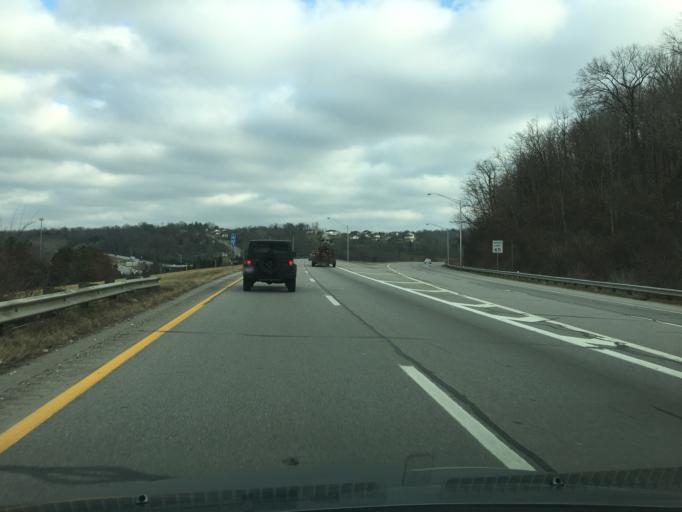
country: US
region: Ohio
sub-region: Hamilton County
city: Miamitown
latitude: 39.2144
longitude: -84.6833
